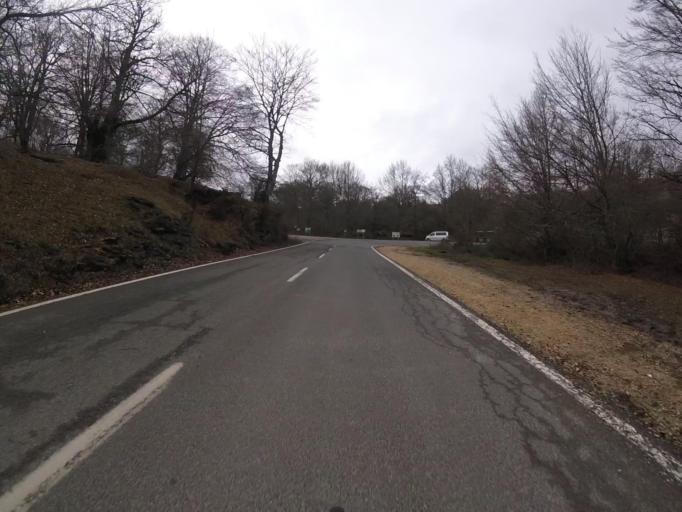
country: ES
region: Navarre
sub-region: Provincia de Navarra
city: Eulate
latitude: 42.7951
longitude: -2.1459
